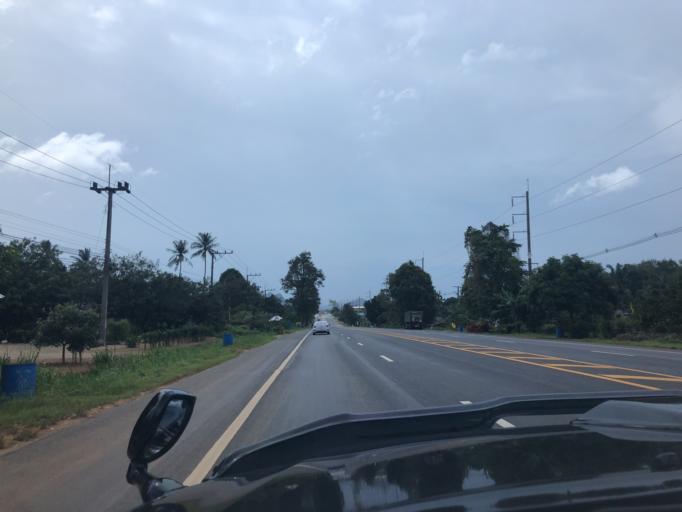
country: TH
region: Phangnga
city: Ban Ao Nang
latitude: 8.2080
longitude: 98.8143
